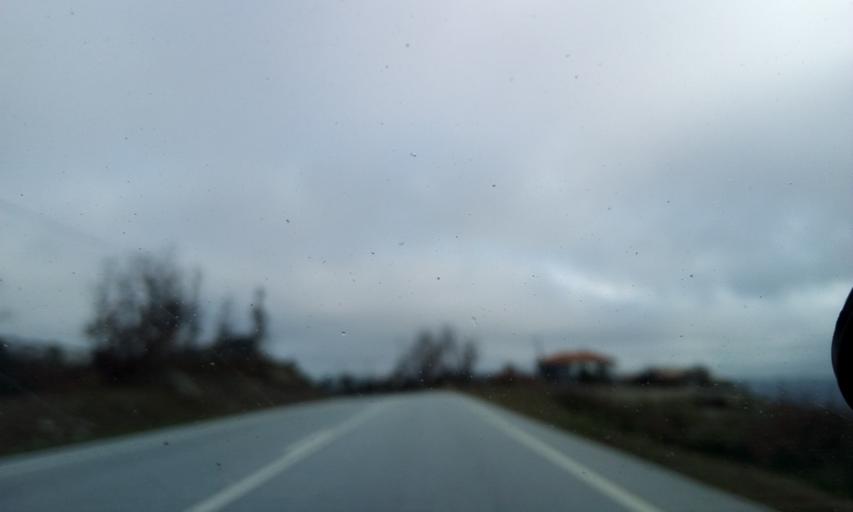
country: PT
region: Guarda
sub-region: Fornos de Algodres
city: Fornos de Algodres
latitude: 40.6745
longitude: -7.4727
